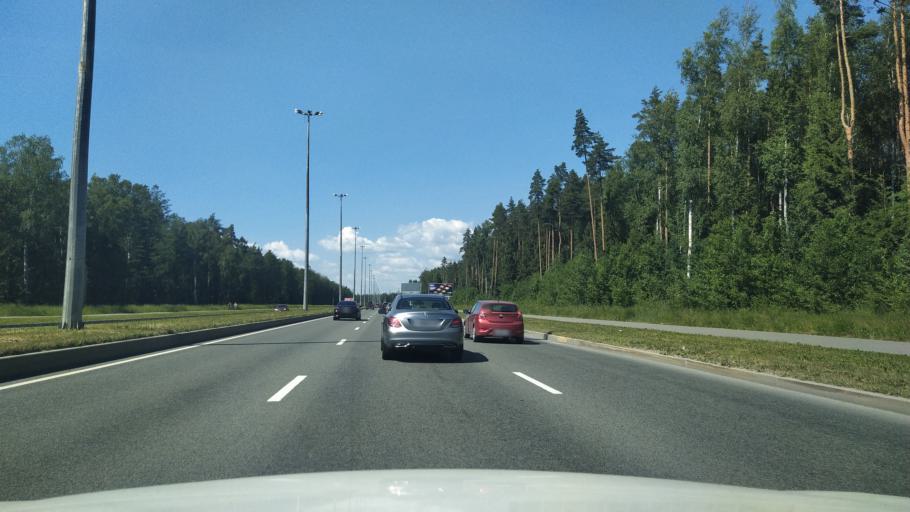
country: RU
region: Leningrad
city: Untolovo
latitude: 60.0541
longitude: 30.2257
